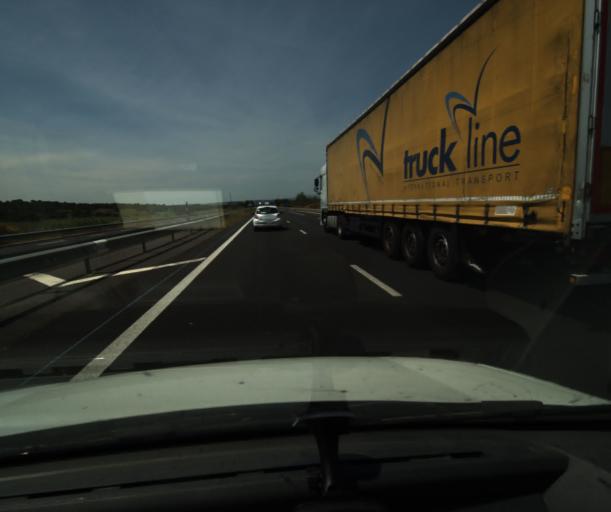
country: FR
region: Languedoc-Roussillon
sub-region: Departement de l'Aude
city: Bizanet
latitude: 43.1575
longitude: 2.8582
